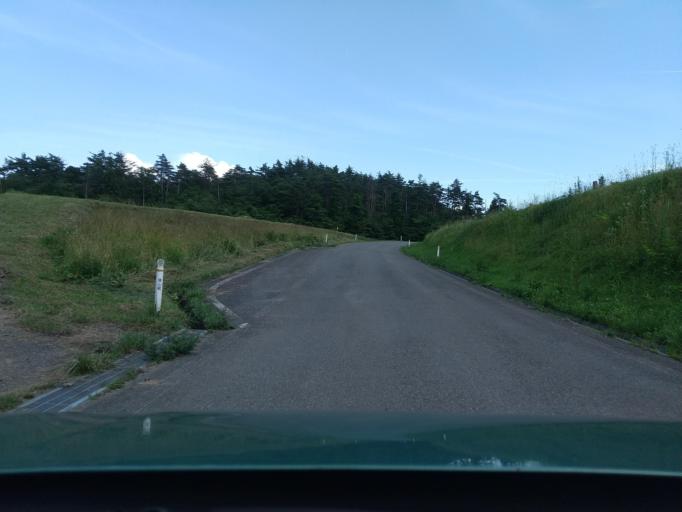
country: JP
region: Iwate
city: Ichinoseki
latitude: 39.0084
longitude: 141.2245
